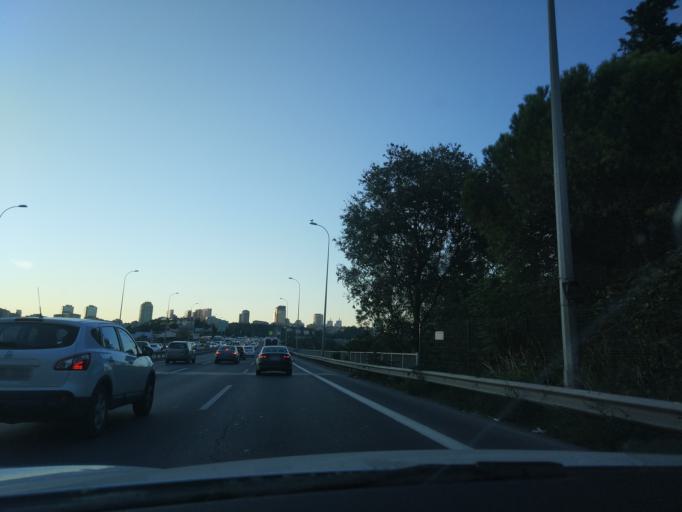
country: TR
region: Istanbul
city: UEskuedar
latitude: 41.0543
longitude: 29.0248
